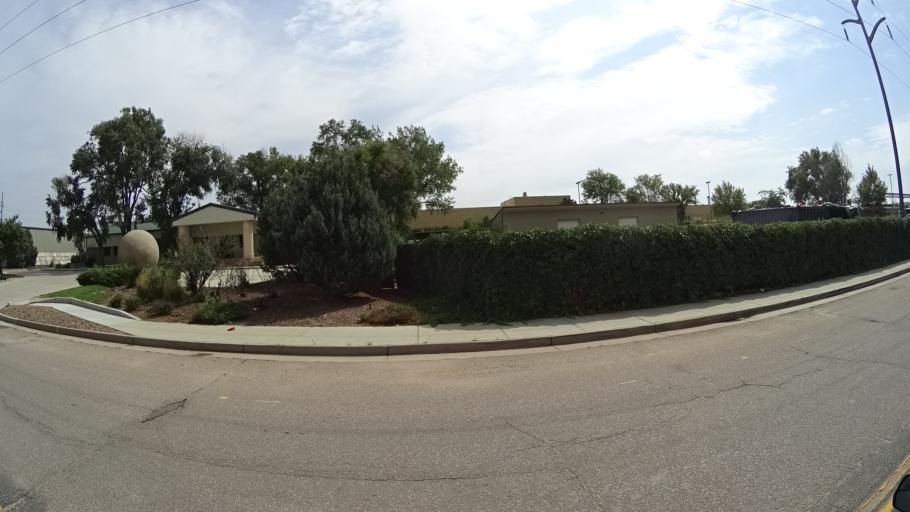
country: US
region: Colorado
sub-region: El Paso County
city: Colorado Springs
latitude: 38.8846
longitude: -104.8226
